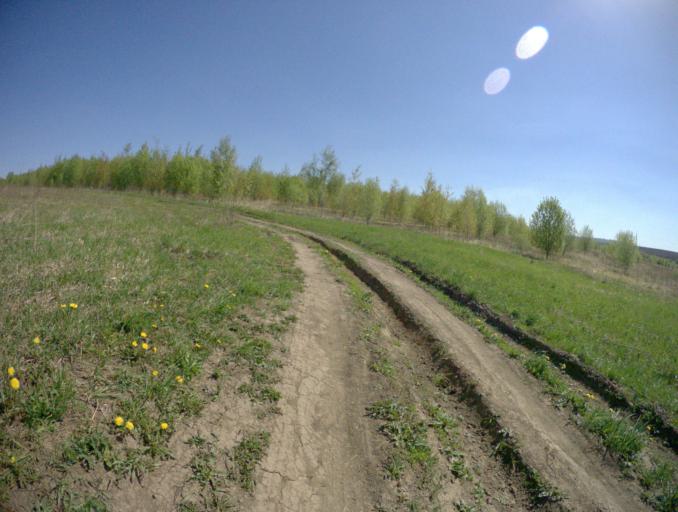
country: RU
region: Vladimir
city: Vladimir
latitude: 56.2897
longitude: 40.3606
